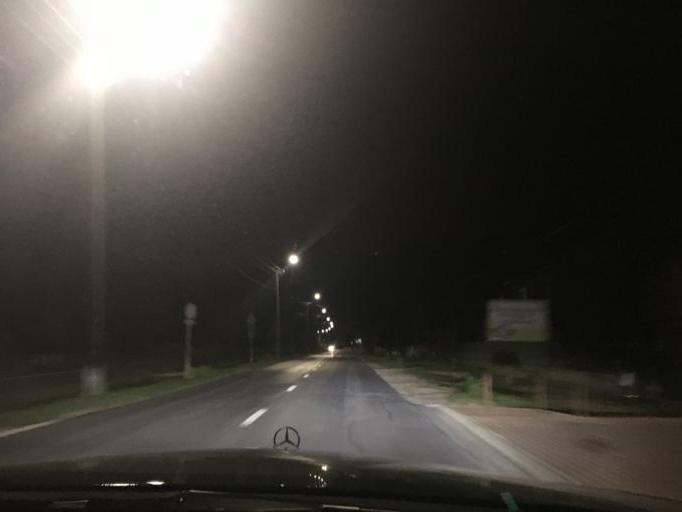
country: HU
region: Hajdu-Bihar
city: Hosszupalyi
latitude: 47.3961
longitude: 21.7290
